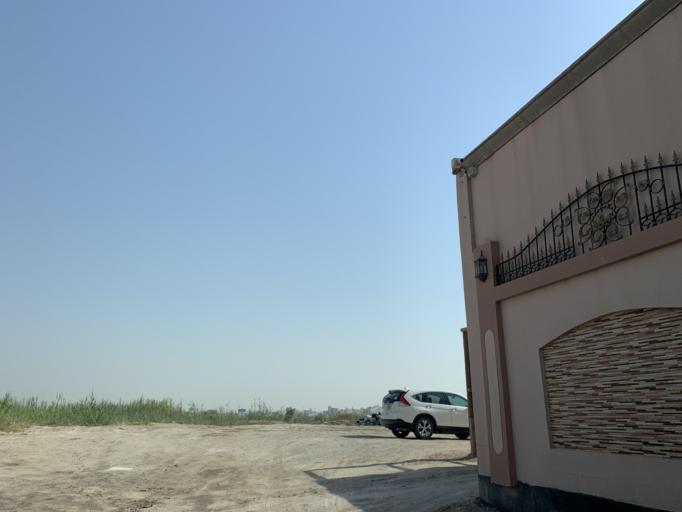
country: BH
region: Manama
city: Jidd Hafs
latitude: 26.1981
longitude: 50.5157
